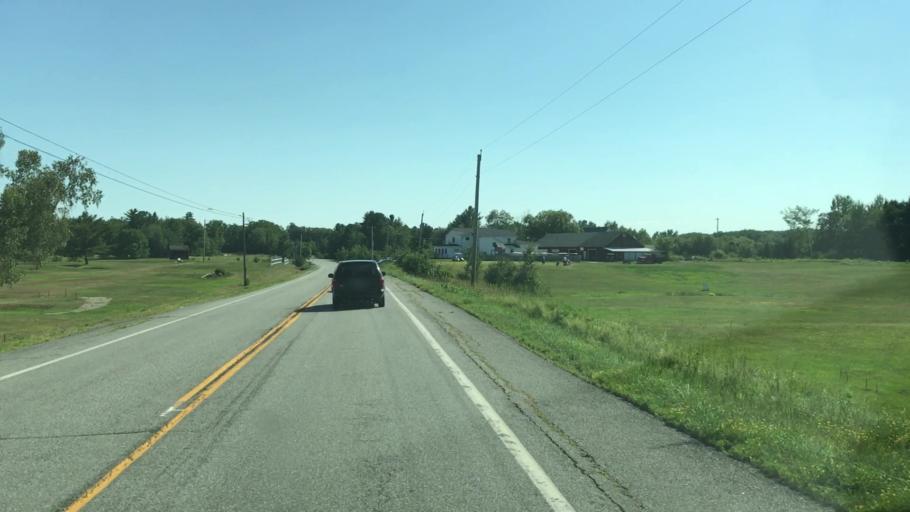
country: US
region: Maine
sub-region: Penobscot County
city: Enfield
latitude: 45.2988
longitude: -68.6185
